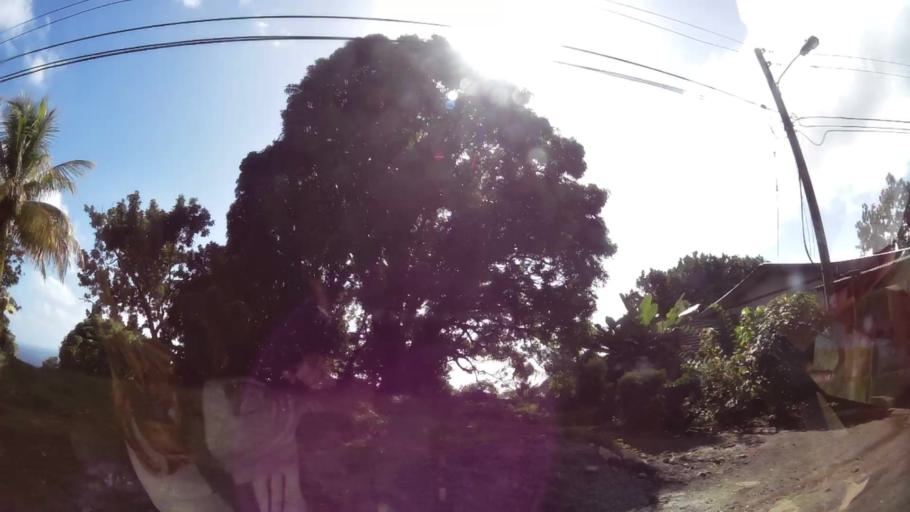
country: DM
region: Saint David
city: Castle Bruce
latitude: 15.4886
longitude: -61.2529
